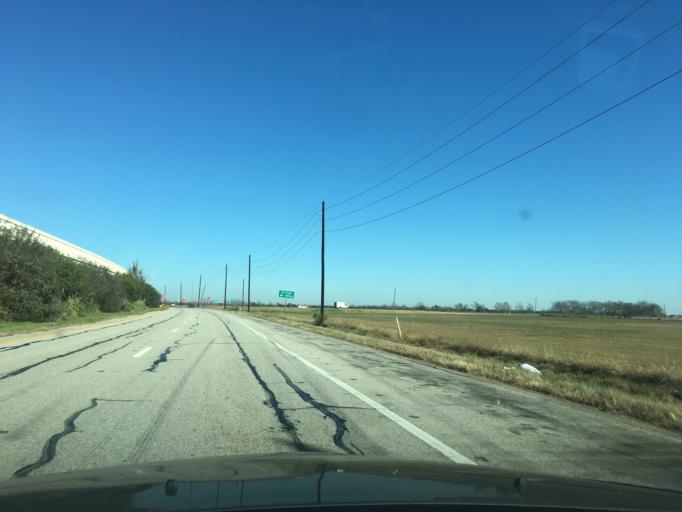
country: US
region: Texas
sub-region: Fort Bend County
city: Pleak
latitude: 29.4929
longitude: -95.9133
